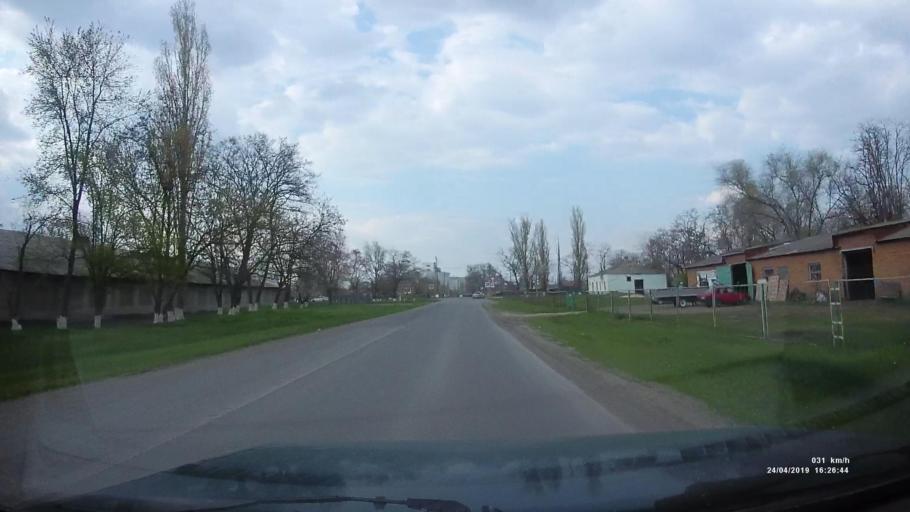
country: RU
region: Rostov
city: Orlovskiy
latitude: 46.8622
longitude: 42.0403
